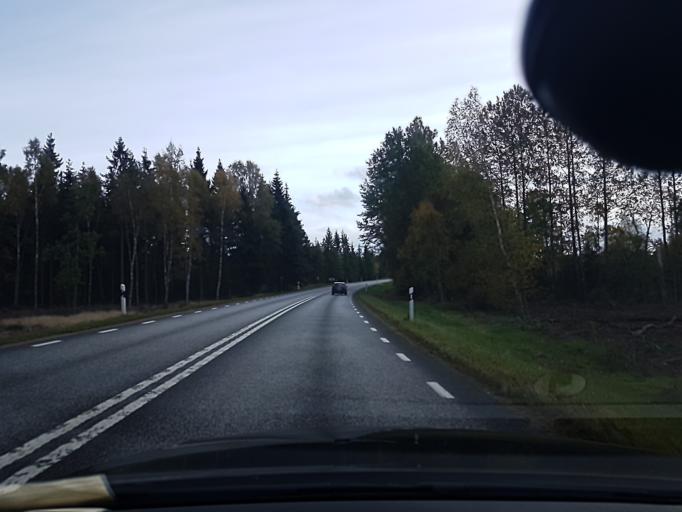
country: SE
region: Joenkoeping
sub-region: Varnamo Kommun
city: Bredaryd
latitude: 57.1758
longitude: 13.7616
